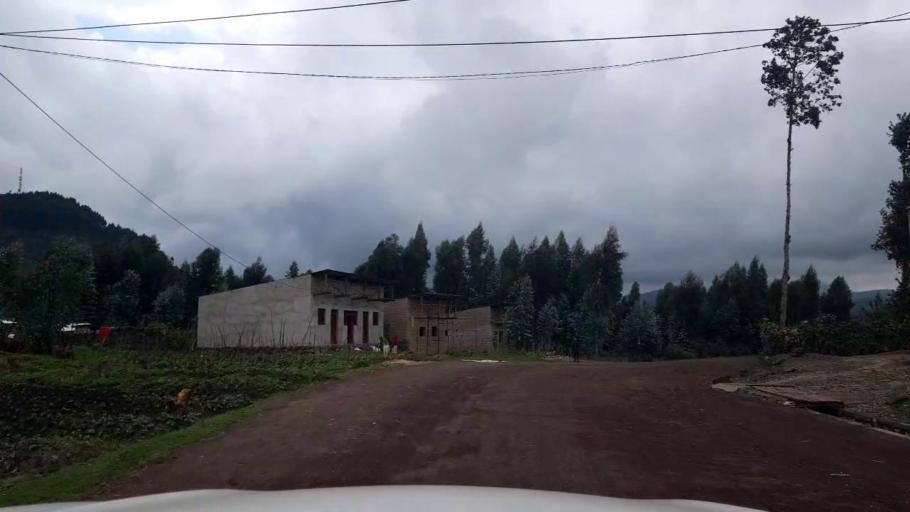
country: RW
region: Northern Province
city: Musanze
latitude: -1.5999
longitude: 29.4525
